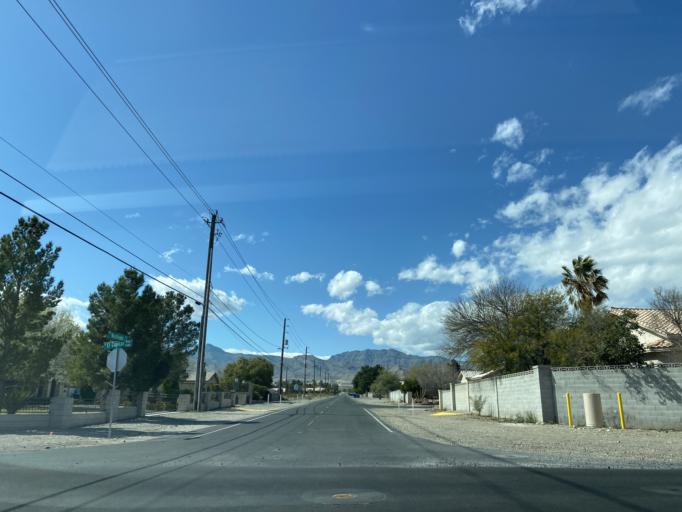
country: US
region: Nevada
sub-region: Clark County
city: Summerlin South
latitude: 36.2556
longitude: -115.2882
